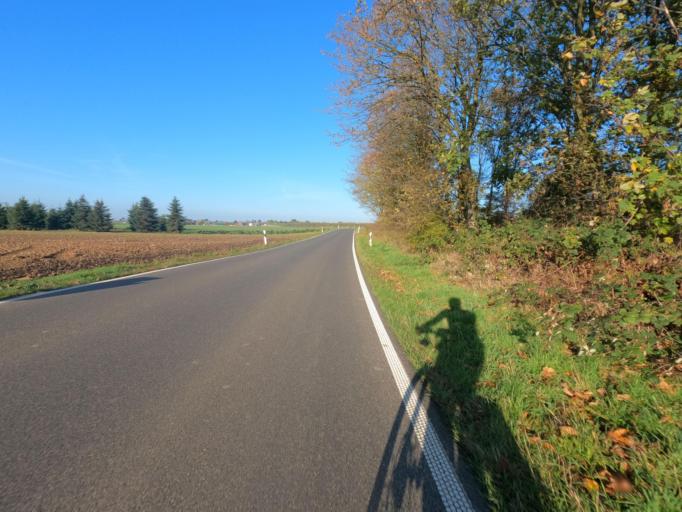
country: DE
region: North Rhine-Westphalia
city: Erkelenz
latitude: 51.0801
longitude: 6.3796
